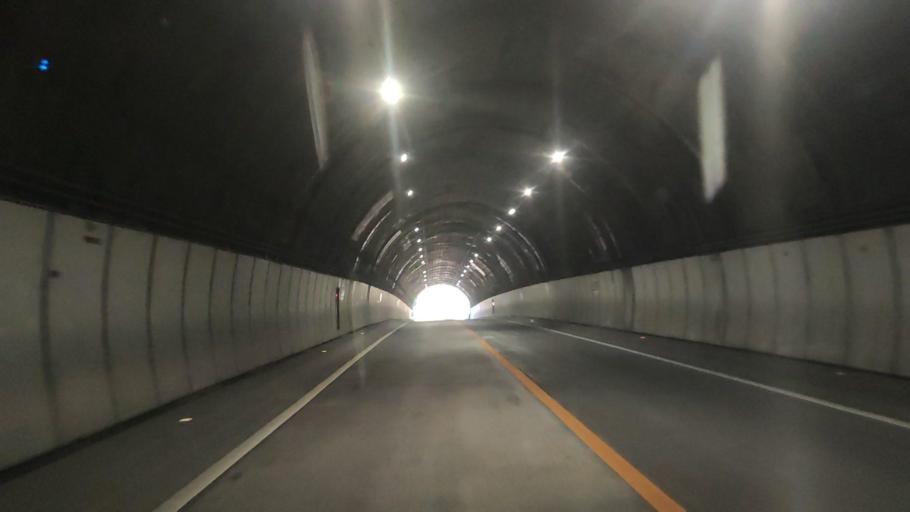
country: JP
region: Oita
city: Tsukumiura
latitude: 32.9987
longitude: 131.7730
